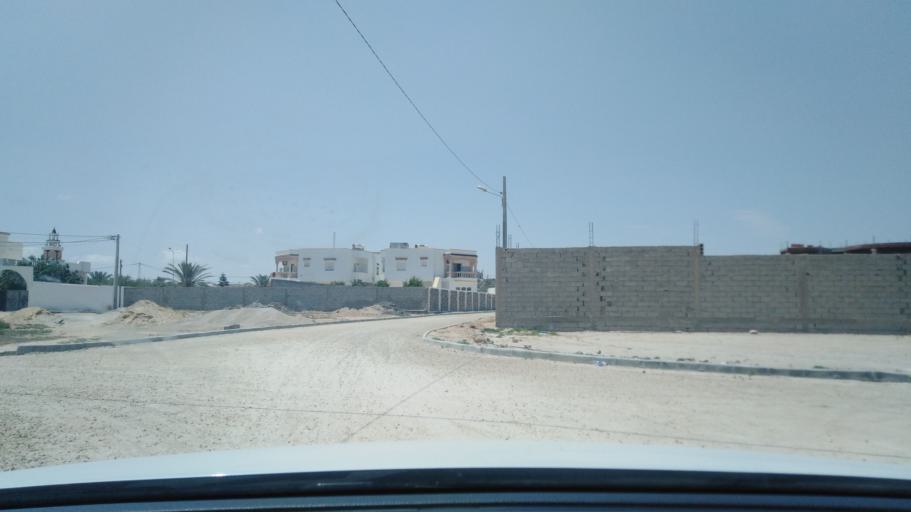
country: TN
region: Qabis
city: Gabes
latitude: 33.9487
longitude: 10.0713
